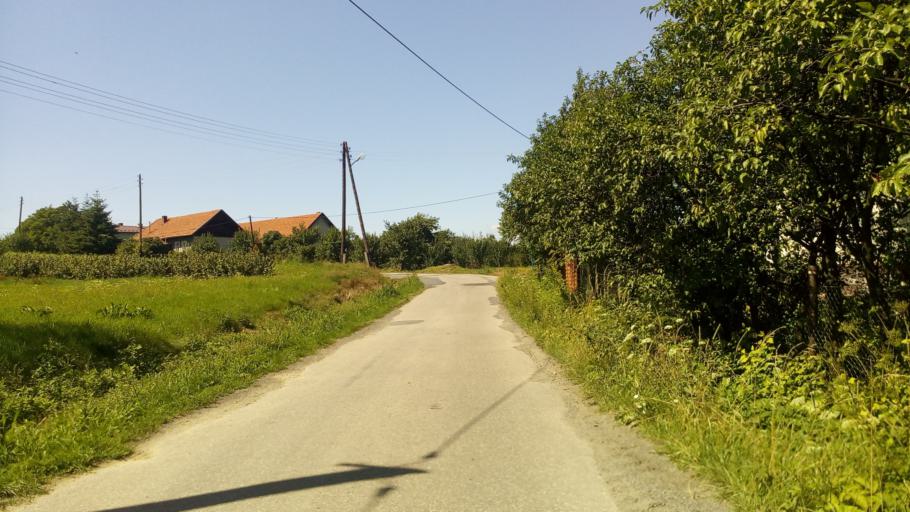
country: PL
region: Lesser Poland Voivodeship
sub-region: Powiat nowosadecki
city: Olszana
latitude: 49.5641
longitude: 20.4990
